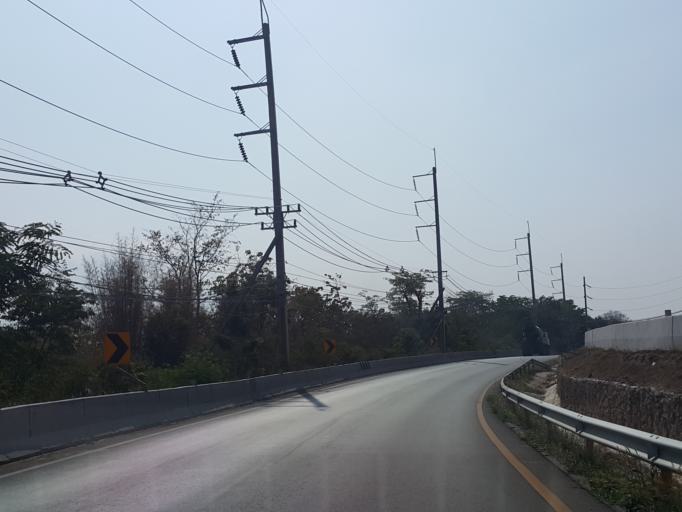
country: TH
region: Chiang Mai
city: Chom Thong
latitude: 18.3707
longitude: 98.6799
